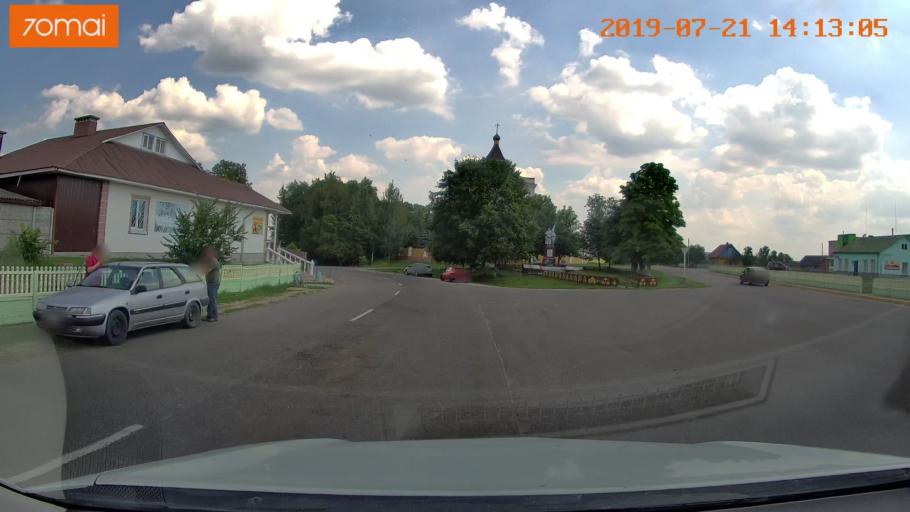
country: BY
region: Grodnenskaya
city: Karelichy
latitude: 53.6510
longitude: 26.1727
